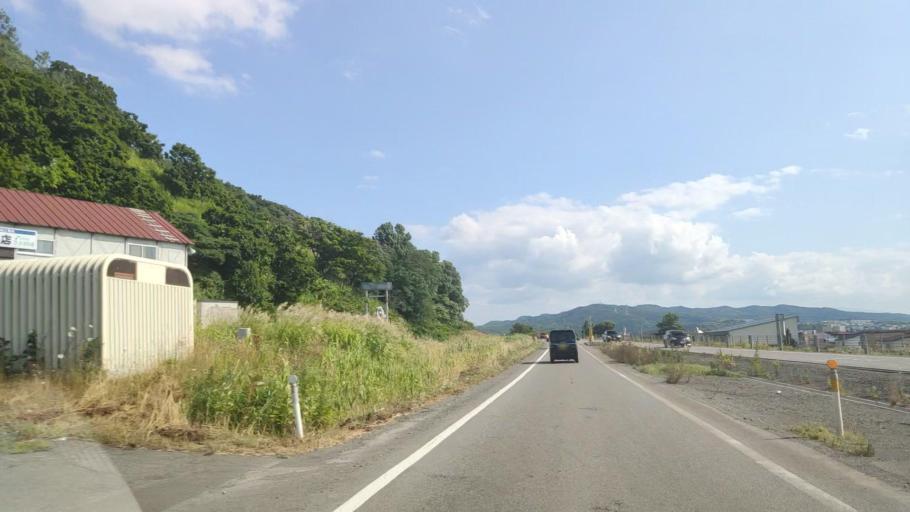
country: JP
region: Hokkaido
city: Rumoi
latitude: 43.9526
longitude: 141.6452
